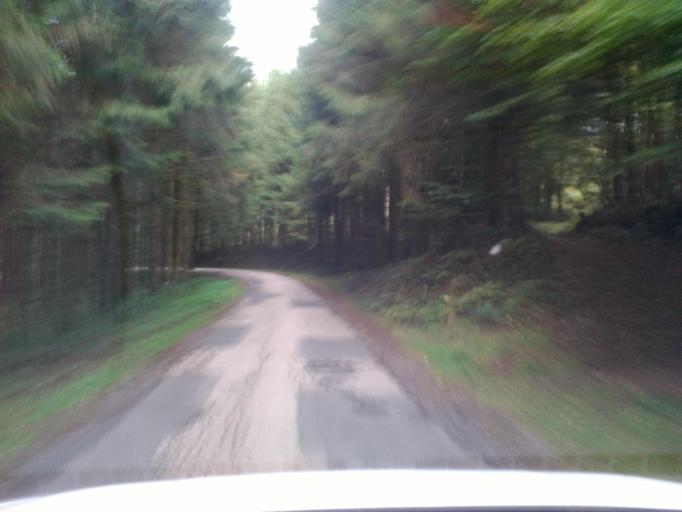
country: FR
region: Lorraine
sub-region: Departement des Vosges
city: Senones
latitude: 48.3999
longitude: 7.0385
